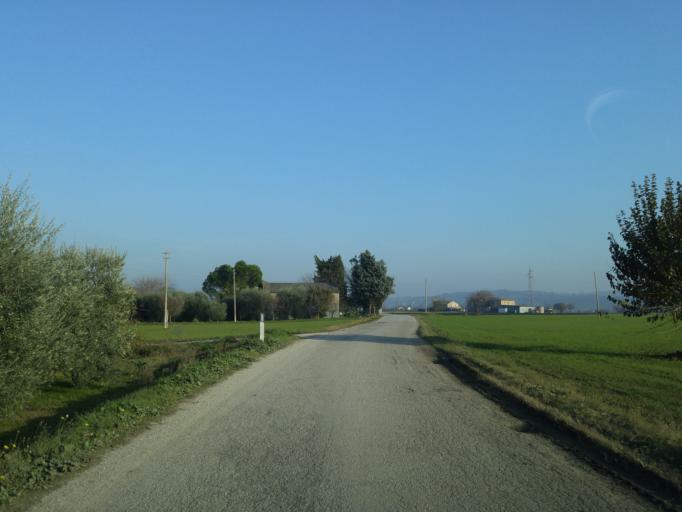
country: IT
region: The Marches
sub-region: Provincia di Pesaro e Urbino
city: Lucrezia
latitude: 43.7767
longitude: 12.9494
